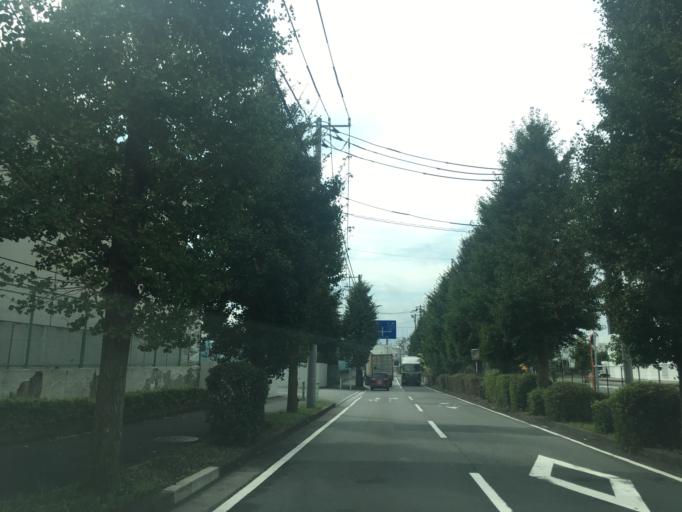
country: JP
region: Tokyo
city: Hachioji
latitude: 35.5861
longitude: 139.3496
